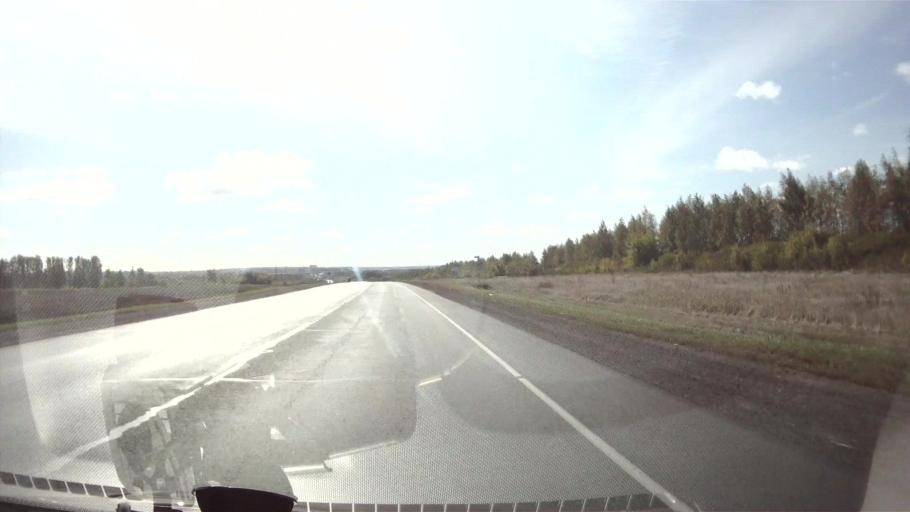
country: RU
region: Ulyanovsk
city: Isheyevka
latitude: 54.3140
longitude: 48.2340
